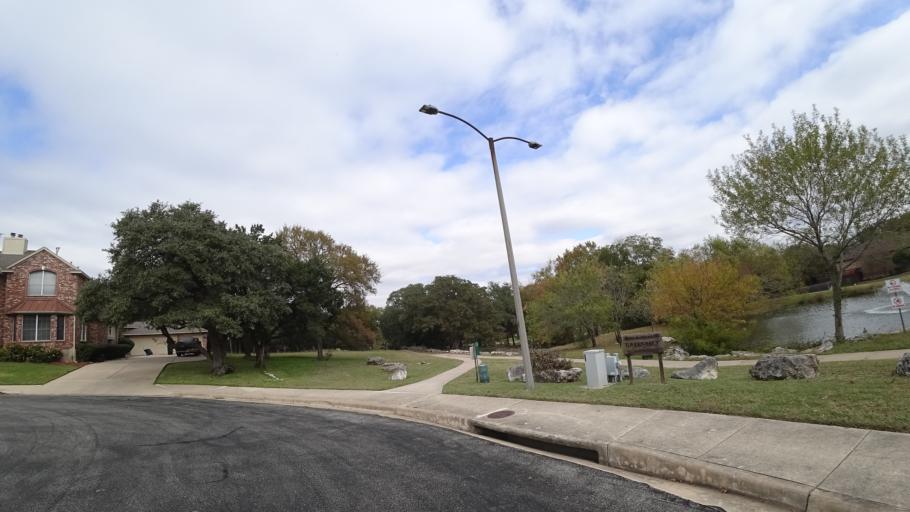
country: US
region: Texas
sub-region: Williamson County
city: Brushy Creek
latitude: 30.5171
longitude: -97.7427
